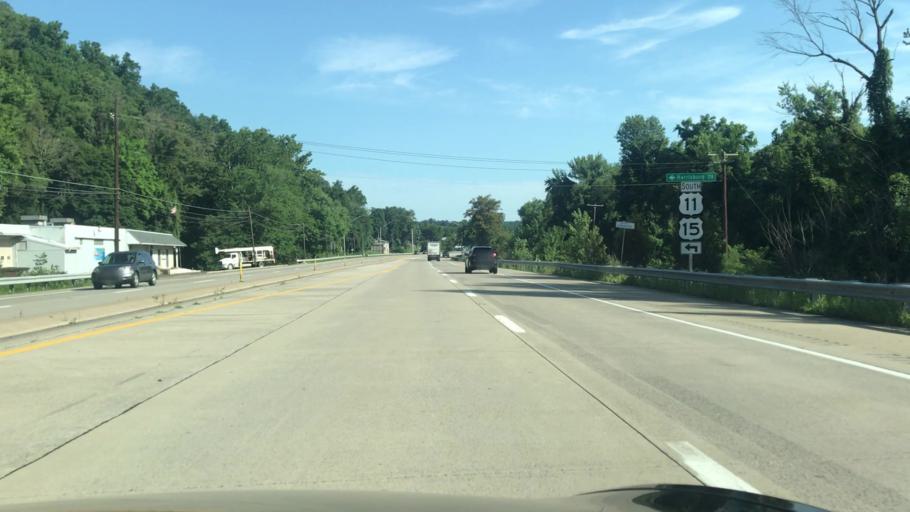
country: US
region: Pennsylvania
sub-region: Dauphin County
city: Millersburg
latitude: 40.5604
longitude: -76.9926
